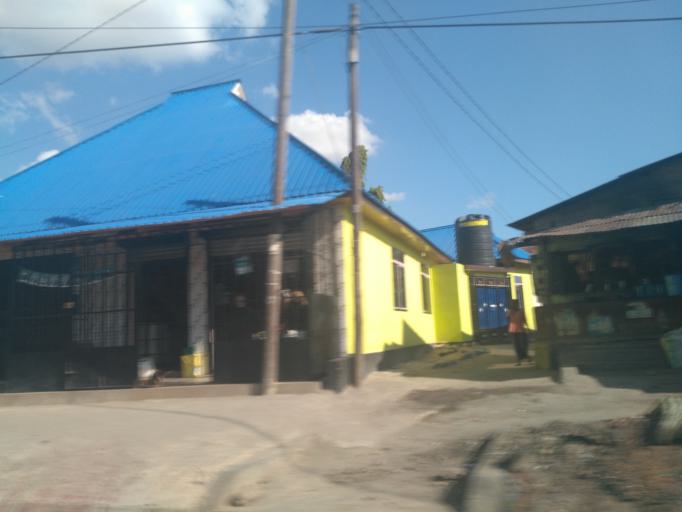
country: TZ
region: Dar es Salaam
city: Dar es Salaam
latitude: -6.8750
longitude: 39.2667
